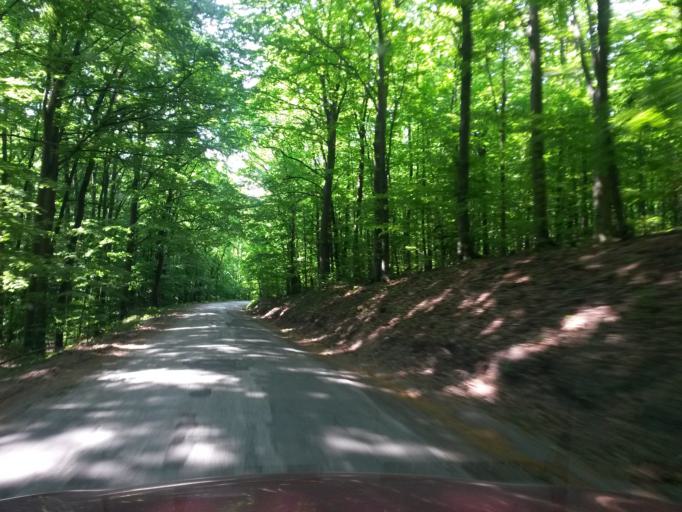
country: SK
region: Kosicky
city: Moldava nad Bodvou
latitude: 48.7197
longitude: 21.0318
